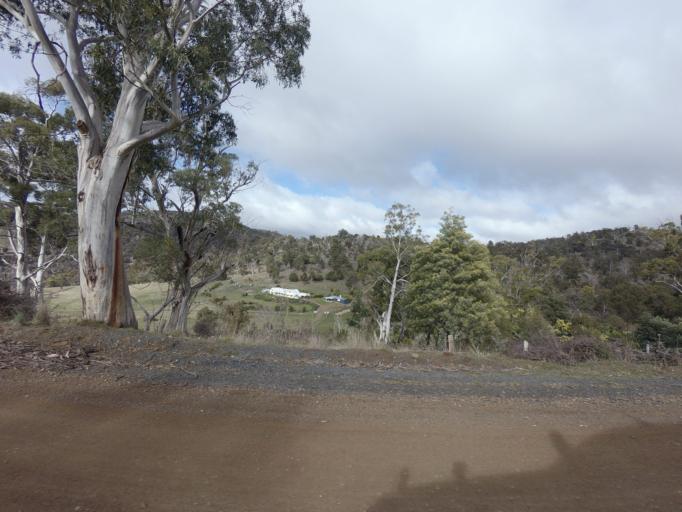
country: AU
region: Tasmania
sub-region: Derwent Valley
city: New Norfolk
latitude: -42.7256
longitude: 146.8716
